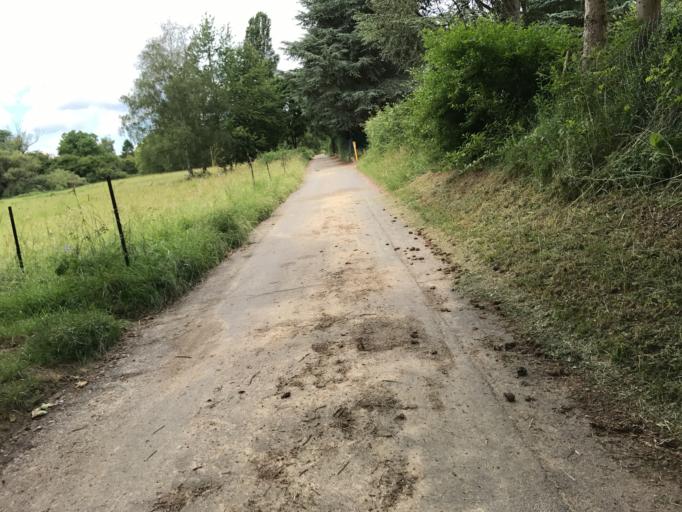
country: DE
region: Hesse
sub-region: Regierungsbezirk Darmstadt
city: Walluf
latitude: 50.0535
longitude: 8.1815
